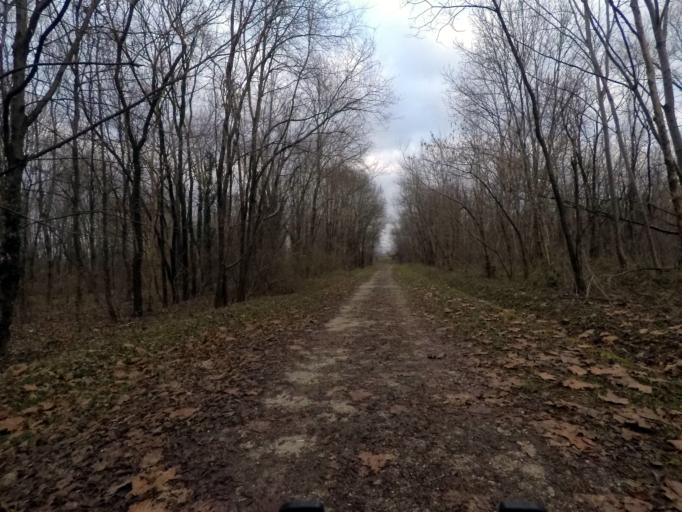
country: IT
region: Friuli Venezia Giulia
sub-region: Provincia di Udine
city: Colugna
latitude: 46.1003
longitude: 13.2027
